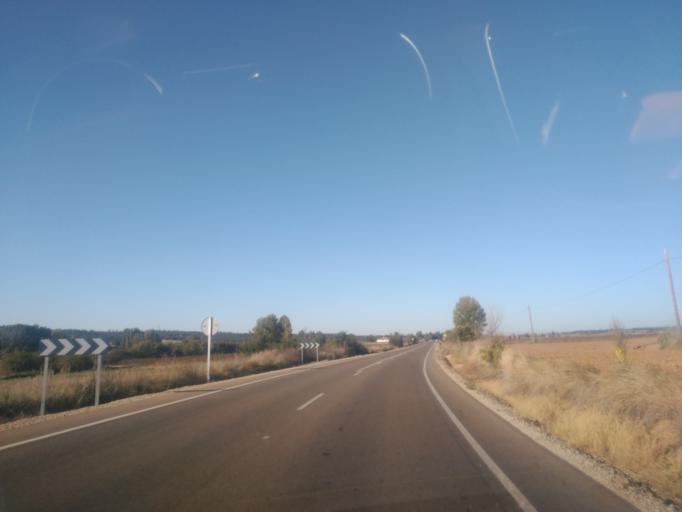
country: ES
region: Castille and Leon
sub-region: Provincia de Burgos
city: Quemada
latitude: 41.6943
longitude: -3.5847
